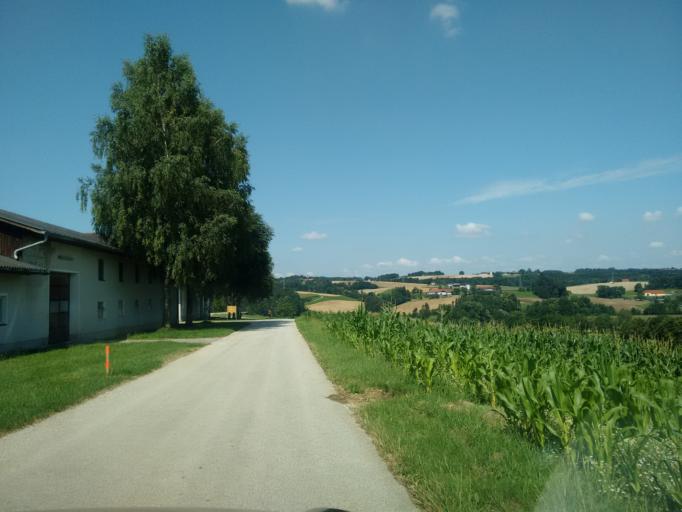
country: AT
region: Upper Austria
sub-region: Politischer Bezirk Kirchdorf an der Krems
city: Kremsmunster
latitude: 48.0128
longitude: 14.1245
